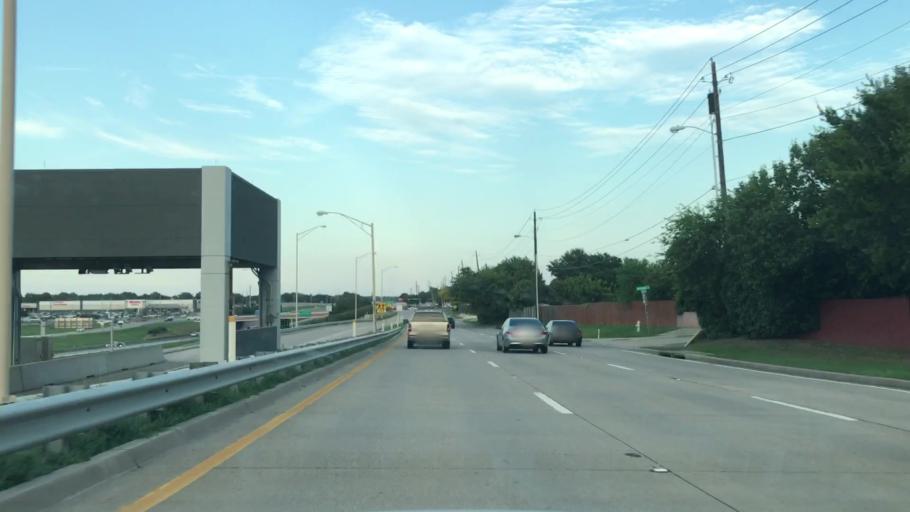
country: US
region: Texas
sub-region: Dallas County
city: Carrollton
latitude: 32.9835
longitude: -96.8943
